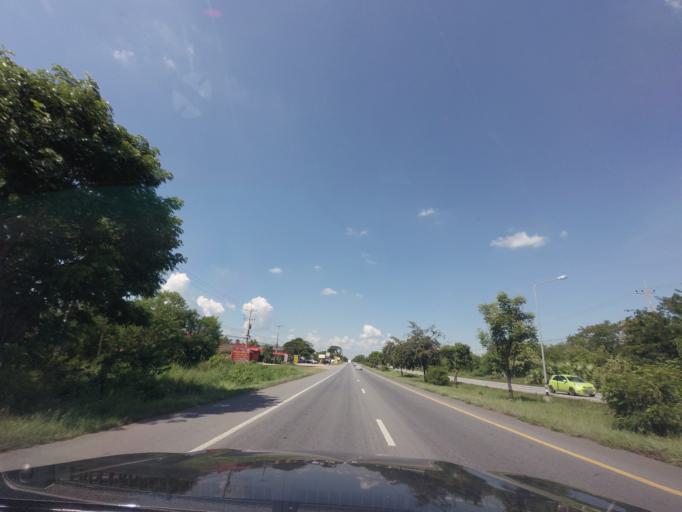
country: TH
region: Nakhon Ratchasima
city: Non Sung
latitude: 15.1513
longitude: 102.3266
